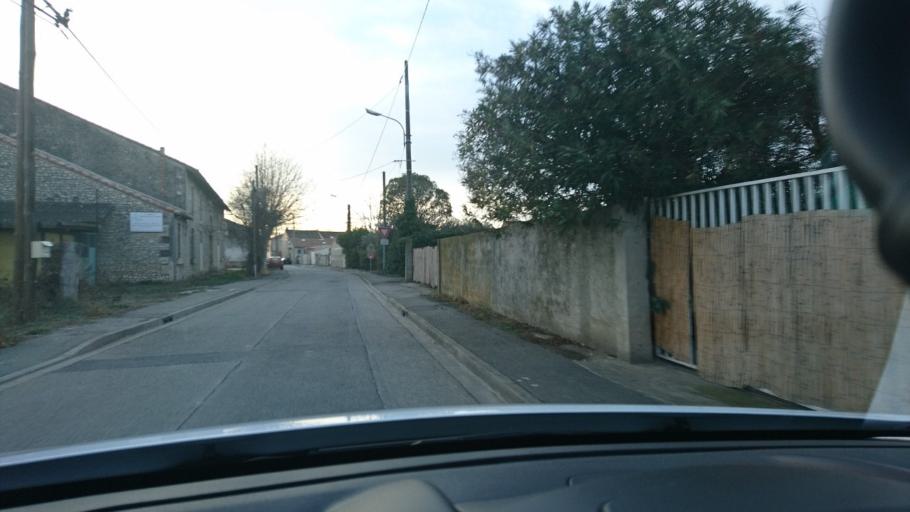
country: FR
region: Provence-Alpes-Cote d'Azur
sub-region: Departement des Bouches-du-Rhone
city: Chateaurenard
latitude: 43.8660
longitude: 4.8377
